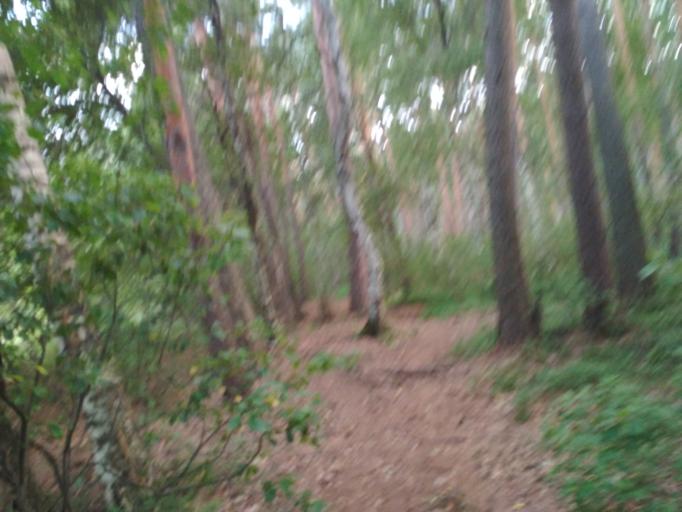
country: RU
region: Rjazan
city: Solotcha
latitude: 54.8295
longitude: 39.9507
